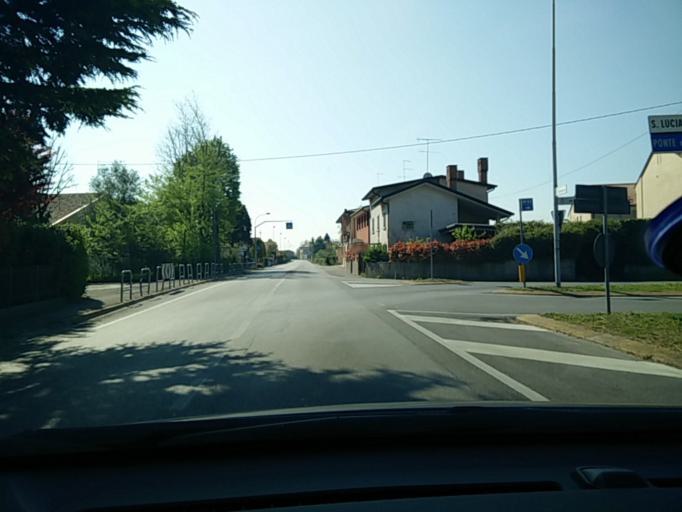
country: IT
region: Veneto
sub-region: Provincia di Treviso
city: Mareno di Piave
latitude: 45.8460
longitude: 12.3131
